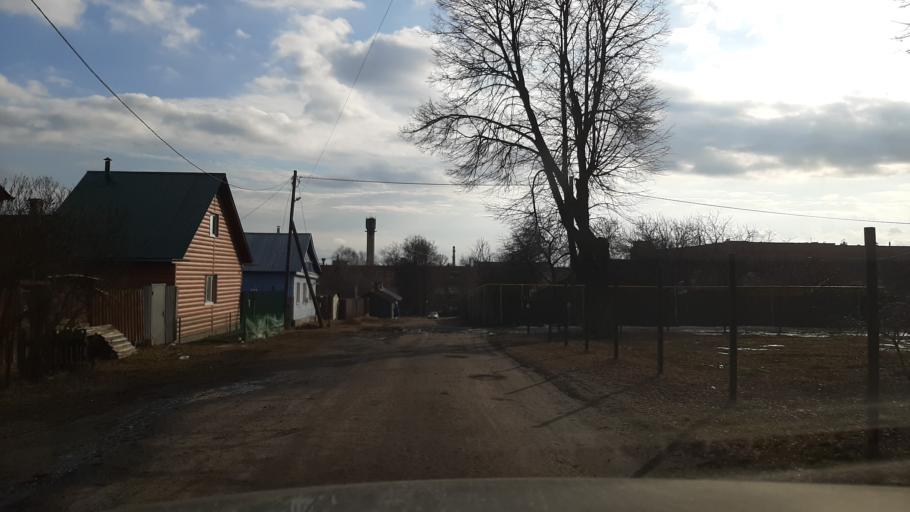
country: RU
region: Ivanovo
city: Teykovo
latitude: 56.8539
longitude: 40.5583
